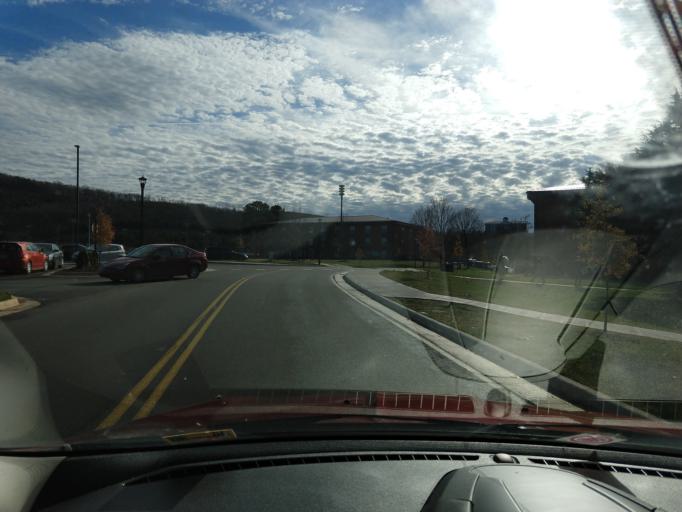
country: US
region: Virginia
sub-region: City of Lynchburg
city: West Lynchburg
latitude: 37.3455
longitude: -79.1850
